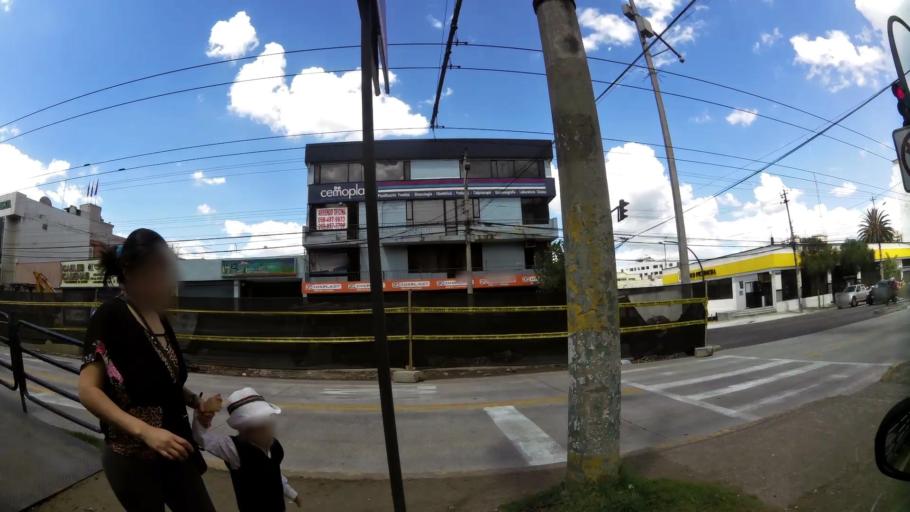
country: EC
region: Pichincha
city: Quito
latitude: -0.1916
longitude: -78.4933
